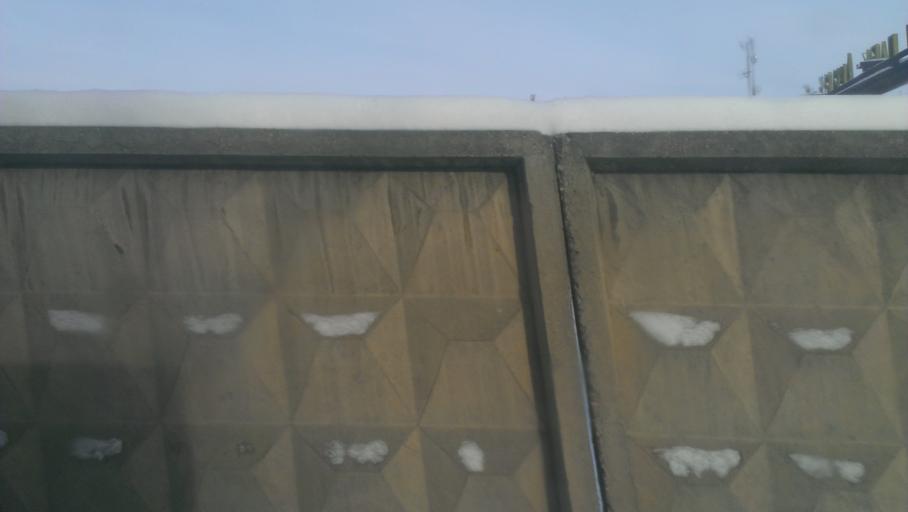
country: RU
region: Altai Krai
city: Nauchnyy Gorodok
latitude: 53.4212
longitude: 83.5221
